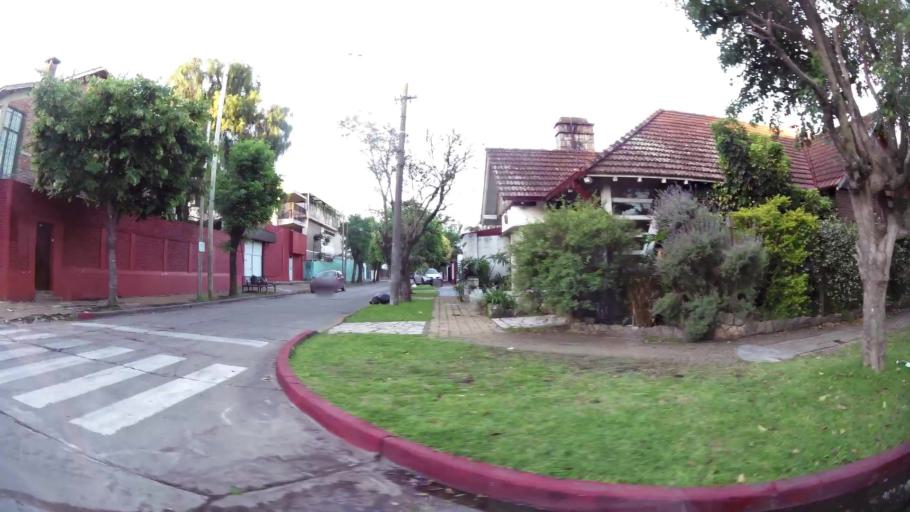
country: AR
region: Buenos Aires
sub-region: Partido de Moron
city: Moron
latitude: -34.6484
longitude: -58.6345
